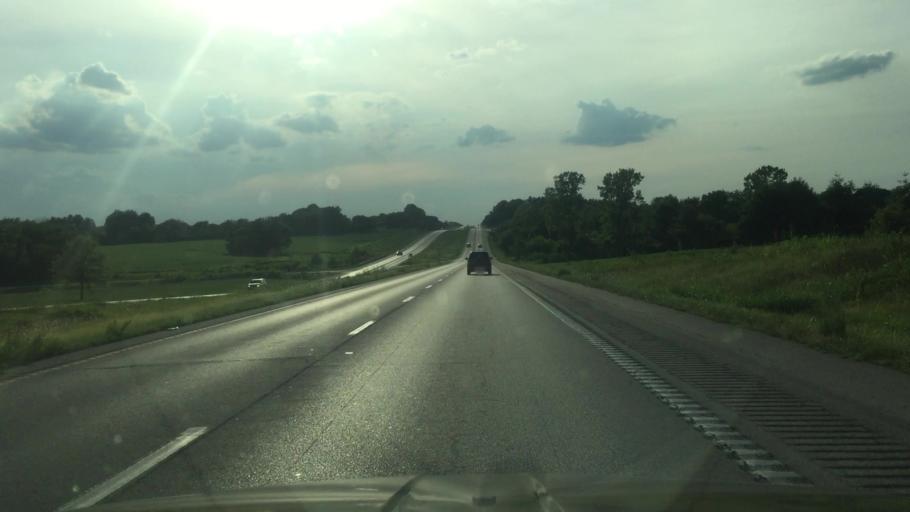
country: US
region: Missouri
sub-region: Jackson County
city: Lone Jack
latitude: 38.8792
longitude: -94.2118
